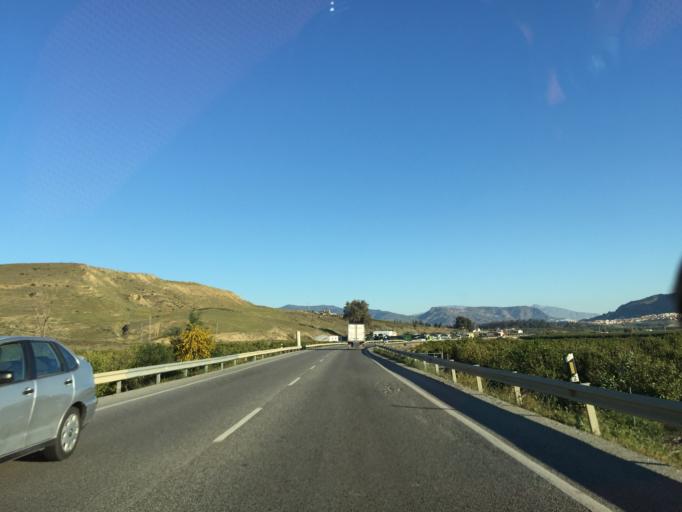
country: ES
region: Andalusia
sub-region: Provincia de Malaga
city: Pizarra
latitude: 36.7378
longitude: -4.7110
